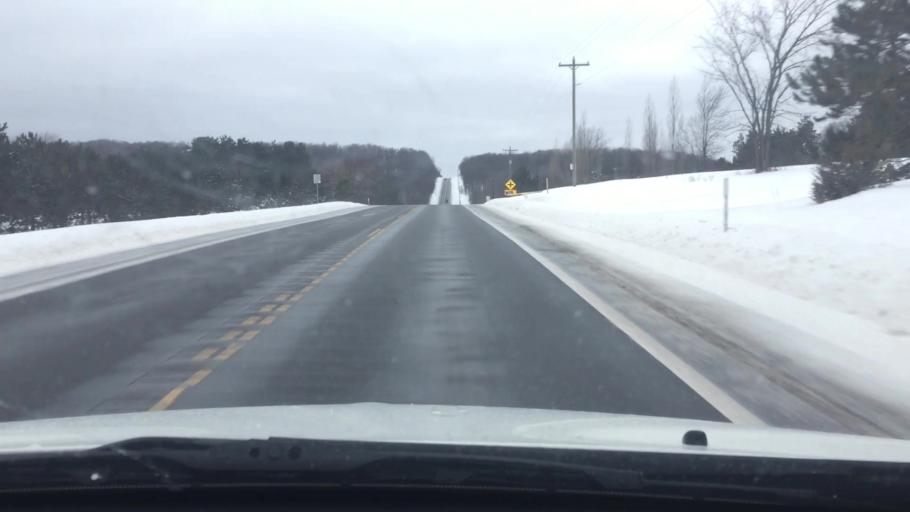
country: US
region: Michigan
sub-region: Charlevoix County
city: Boyne City
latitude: 45.0964
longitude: -84.9960
